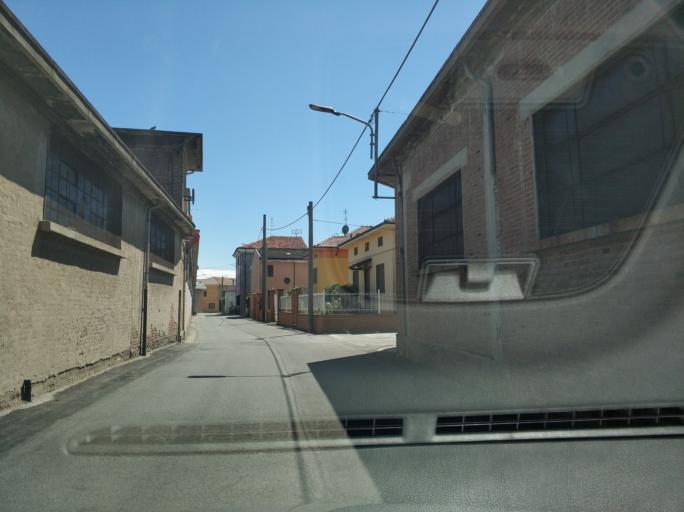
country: IT
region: Piedmont
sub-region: Provincia di Vercelli
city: Cigliano
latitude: 45.3071
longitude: 8.0150
